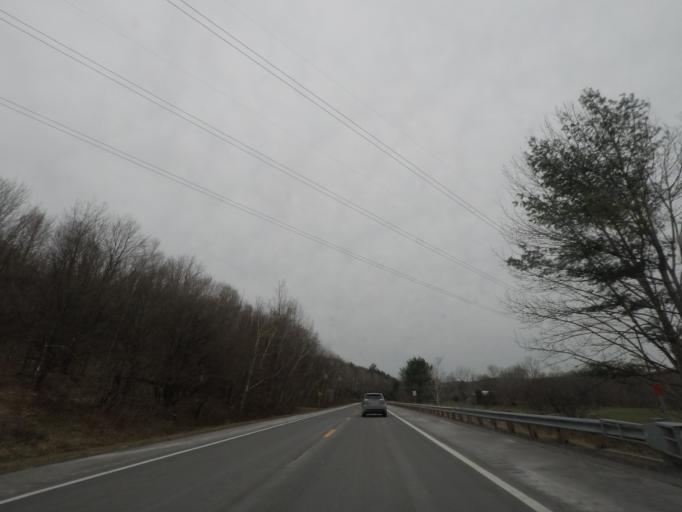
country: US
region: Massachusetts
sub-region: Berkshire County
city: Lanesborough
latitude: 42.5392
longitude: -73.3286
